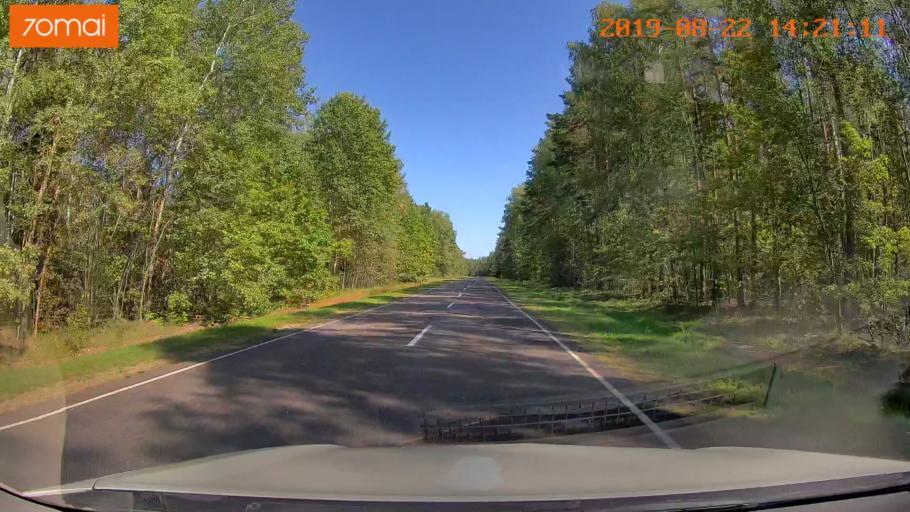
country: BY
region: Mogilev
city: Asipovichy
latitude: 53.2662
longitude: 28.5476
